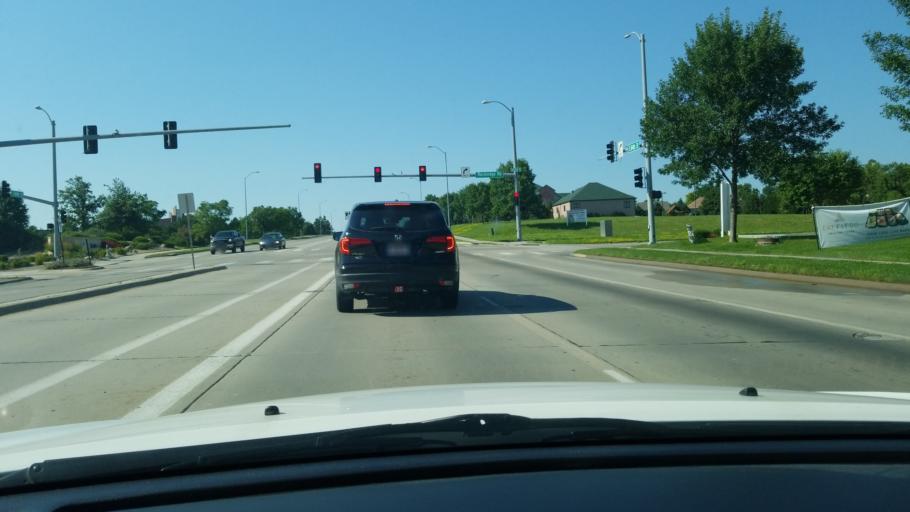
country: US
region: Nebraska
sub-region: Lancaster County
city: Lincoln
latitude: 40.7819
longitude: -96.6061
